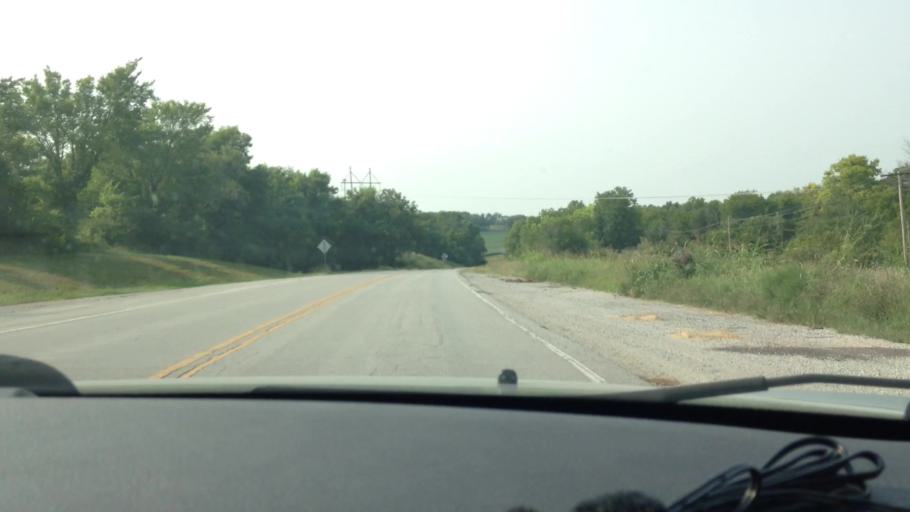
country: US
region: Missouri
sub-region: Platte County
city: Platte City
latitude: 39.3866
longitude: -94.7934
